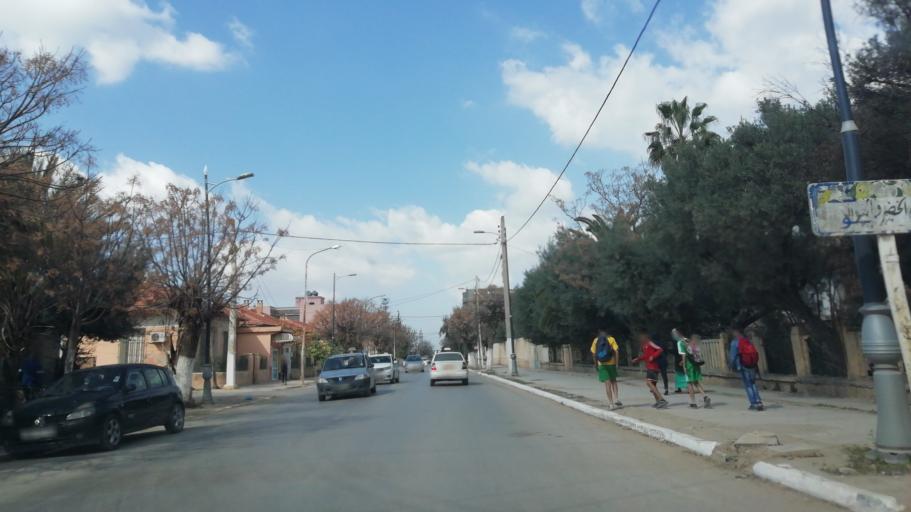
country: DZ
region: Mascara
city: Mascara
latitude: 35.5828
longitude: 0.0698
